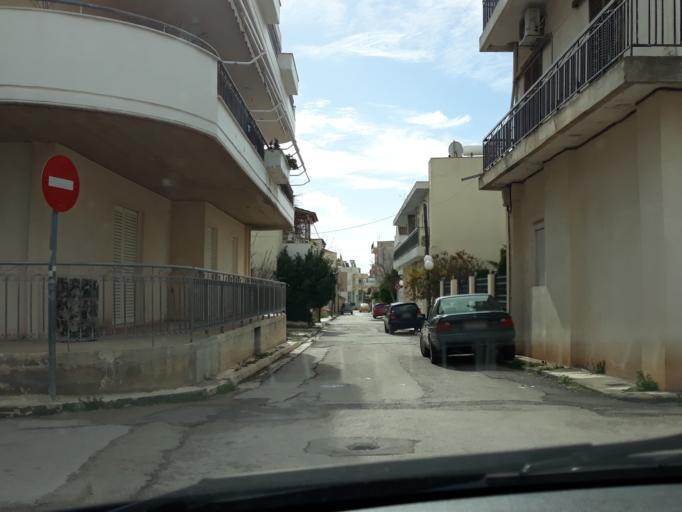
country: GR
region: Attica
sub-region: Nomarchia Dytikis Attikis
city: Ano Liosia
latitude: 38.0814
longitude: 23.7054
